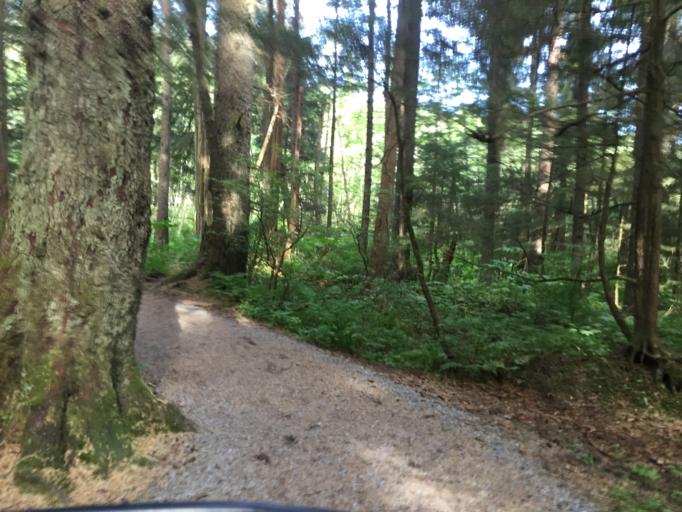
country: US
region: Alaska
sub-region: Sitka City and Borough
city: Sitka
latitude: 57.0490
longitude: -135.3180
